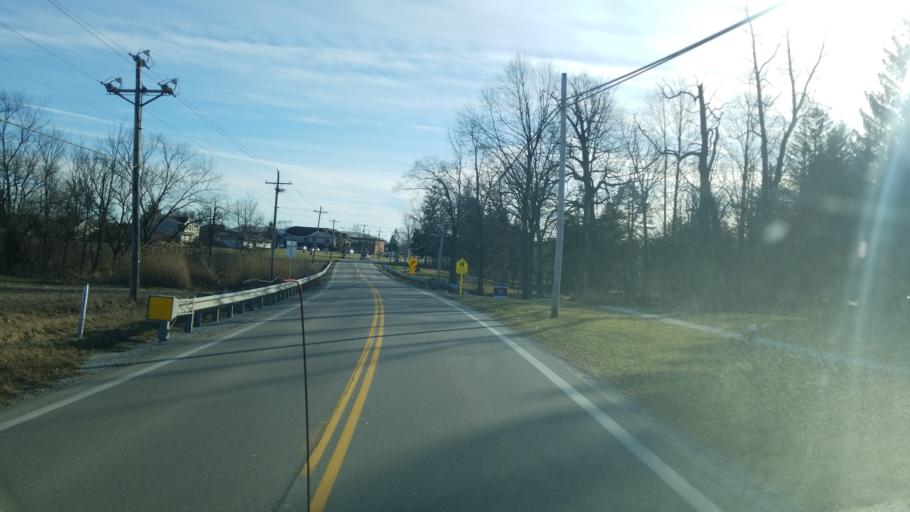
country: US
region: Ohio
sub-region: Sandusky County
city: Green Springs
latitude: 41.2661
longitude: -83.0524
